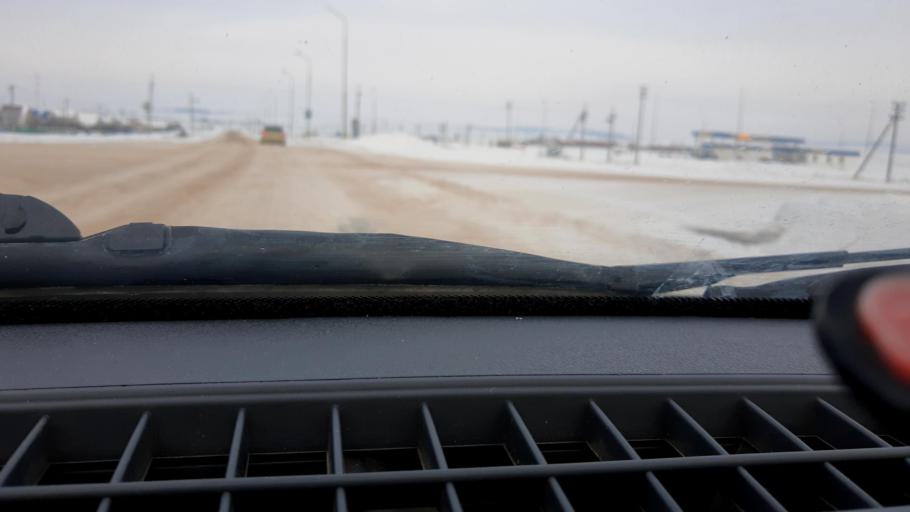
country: RU
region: Bashkortostan
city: Alekseyevka
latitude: 54.6897
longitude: 55.0301
